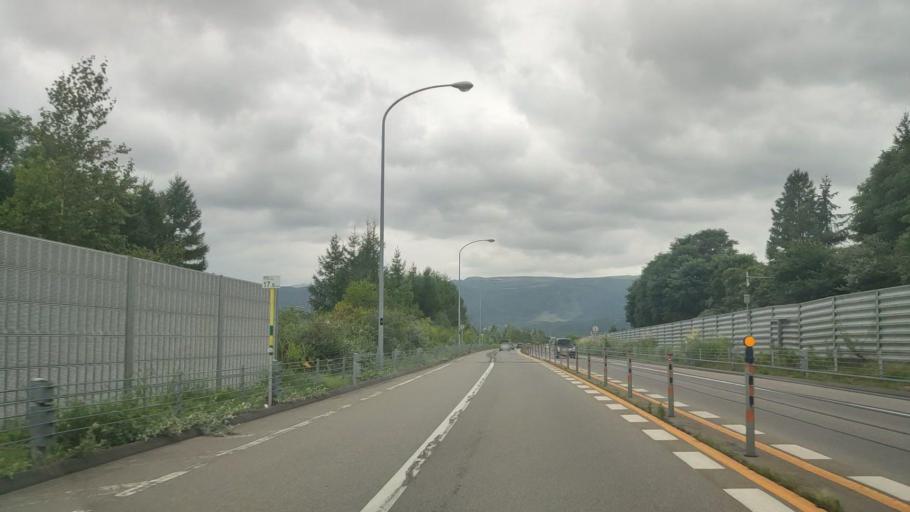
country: JP
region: Hokkaido
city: Nanae
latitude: 41.9155
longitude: 140.6875
